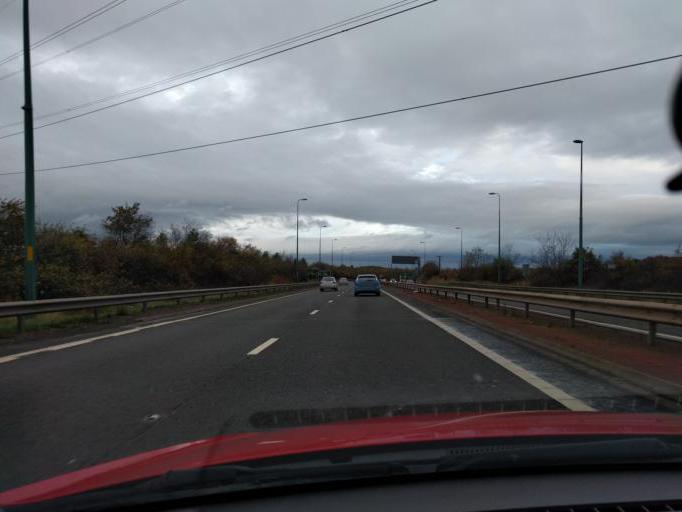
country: GB
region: Scotland
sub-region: Midlothian
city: Dalkeith
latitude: 55.9181
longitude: -3.0641
